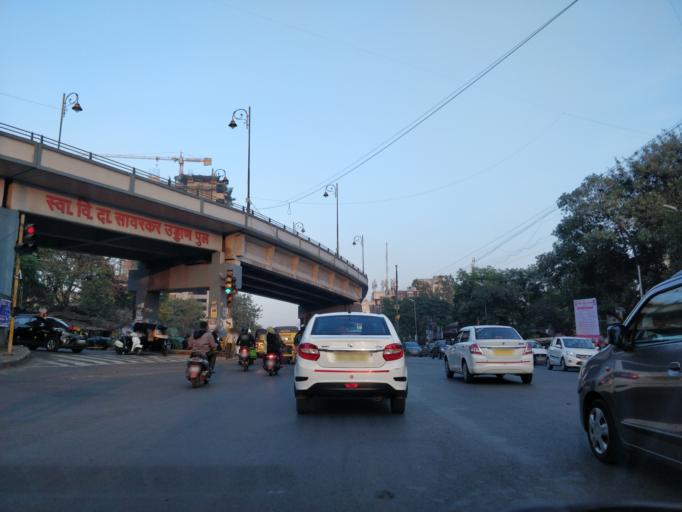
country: IN
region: Maharashtra
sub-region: Pune Division
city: Pune
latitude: 18.5057
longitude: 73.8249
